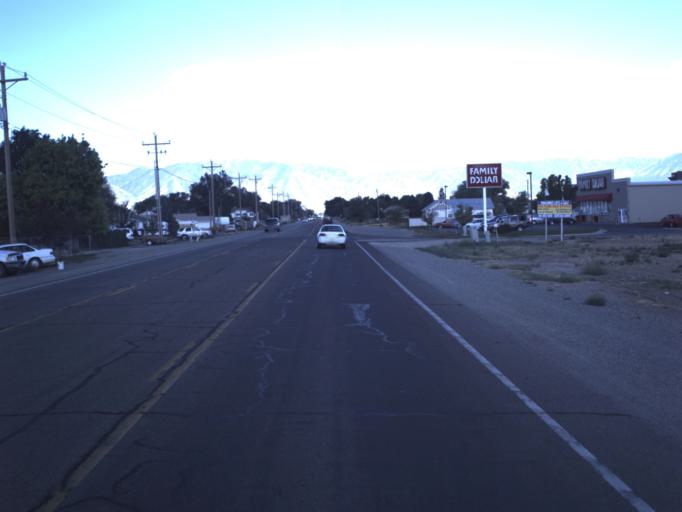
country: US
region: Utah
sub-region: Tooele County
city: Grantsville
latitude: 40.5997
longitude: -112.4406
